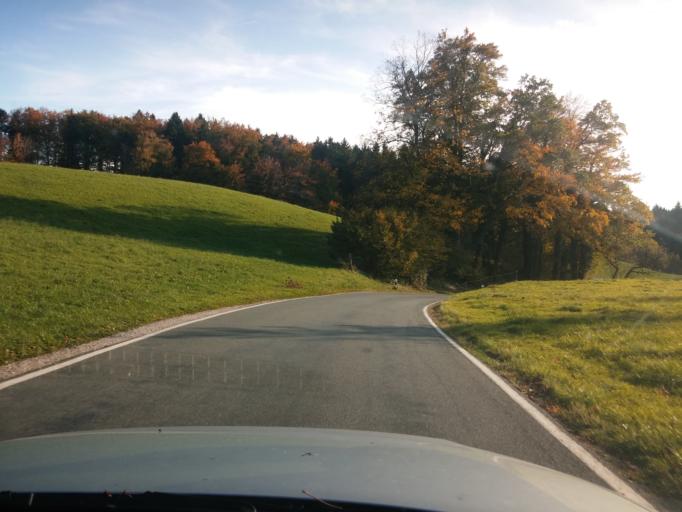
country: DE
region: Bavaria
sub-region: Upper Bavaria
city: Dietramszell
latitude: 47.8228
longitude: 11.5821
